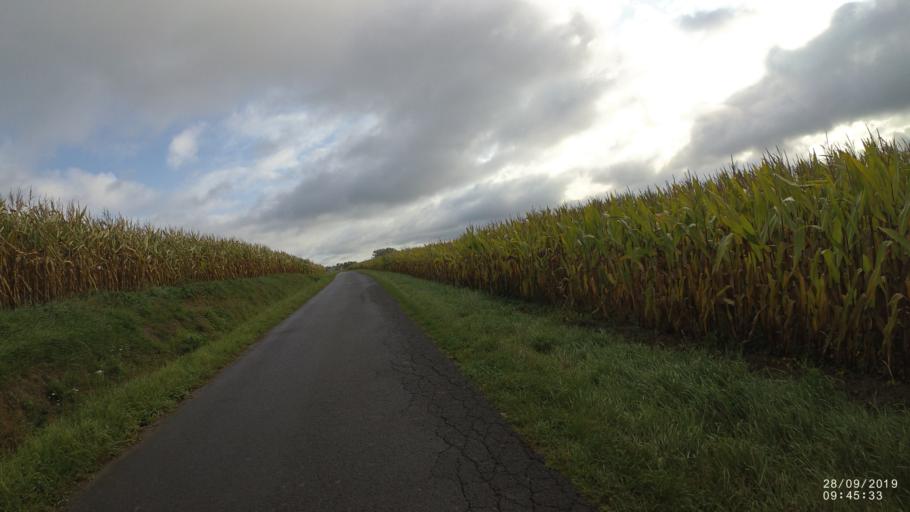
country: BE
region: Wallonia
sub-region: Province du Hainaut
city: Flobecq
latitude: 50.7991
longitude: 3.7318
